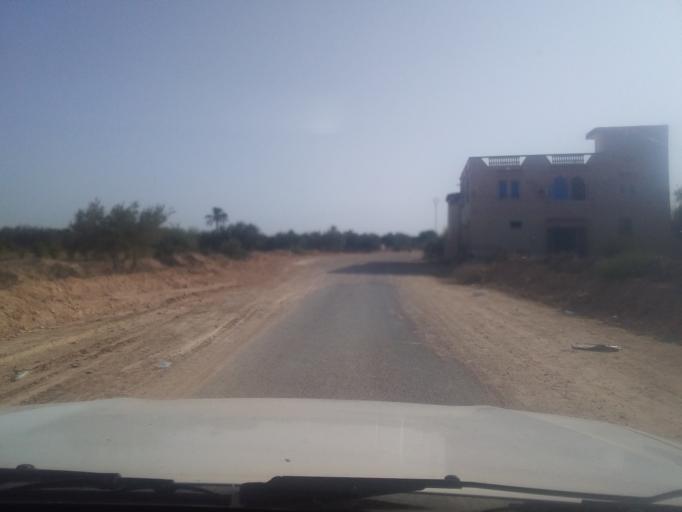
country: TN
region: Qabis
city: Matmata
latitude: 33.6065
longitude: 10.2796
